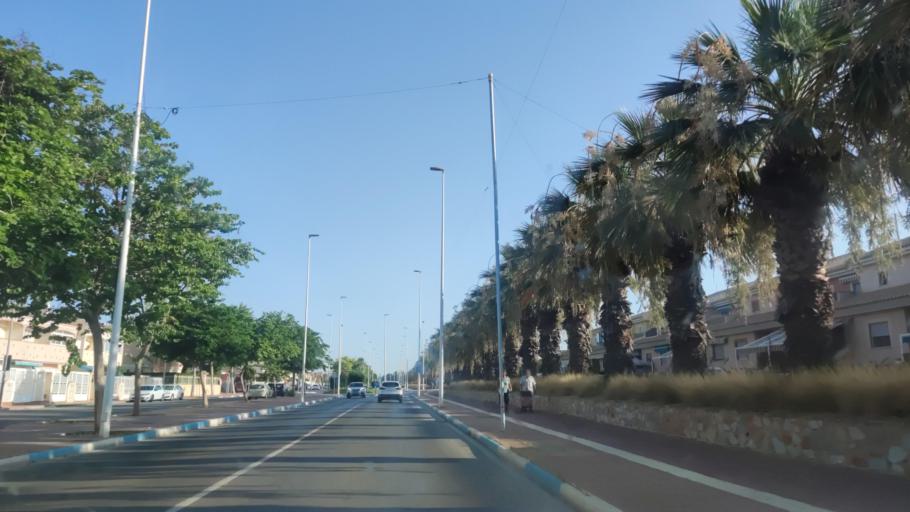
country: ES
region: Murcia
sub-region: Murcia
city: Los Alcazares
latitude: 37.7461
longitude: -0.8540
